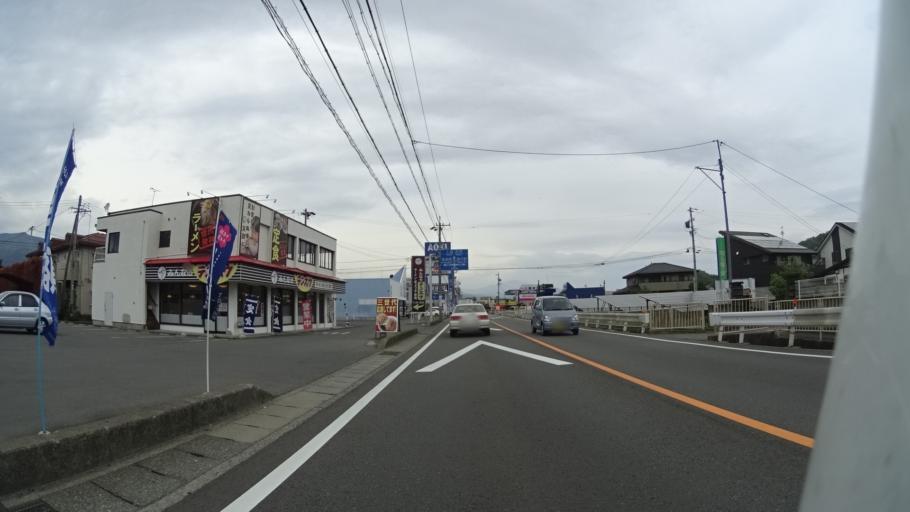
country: JP
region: Nagano
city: Nagano-shi
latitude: 36.5278
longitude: 138.1236
